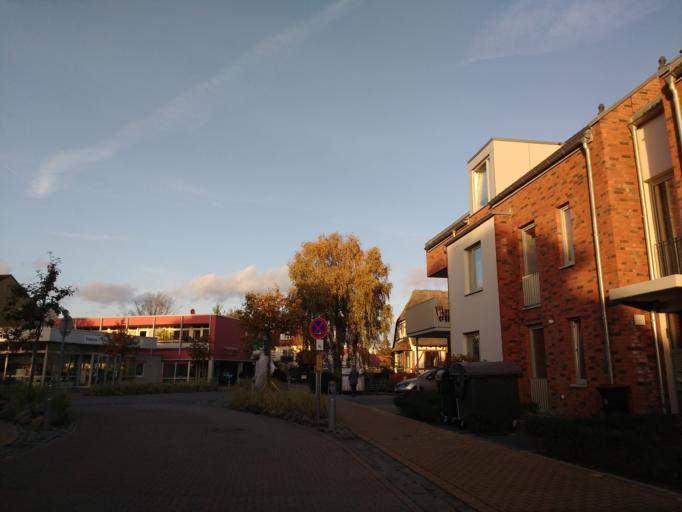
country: DE
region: Schleswig-Holstein
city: Kellenhusen
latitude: 54.1902
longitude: 11.0598
